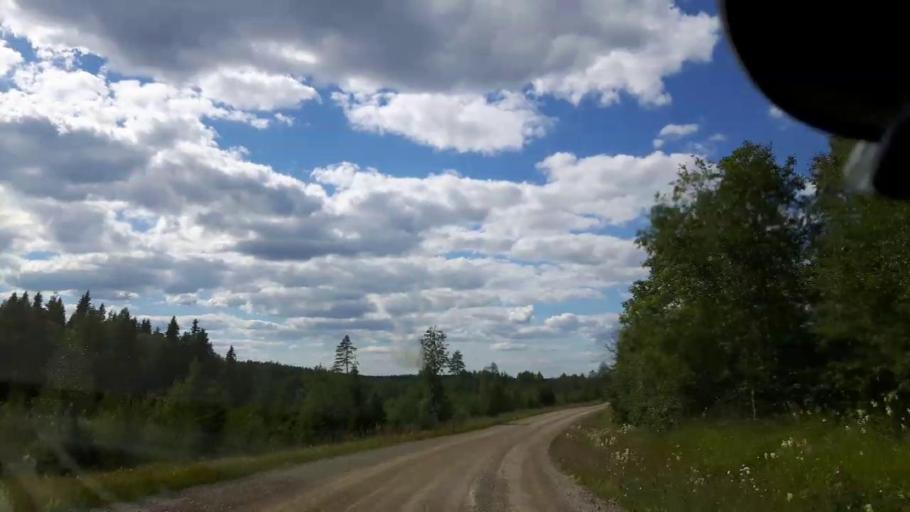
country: SE
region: Jaemtland
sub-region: Braecke Kommun
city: Braecke
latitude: 62.7220
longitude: 15.5483
